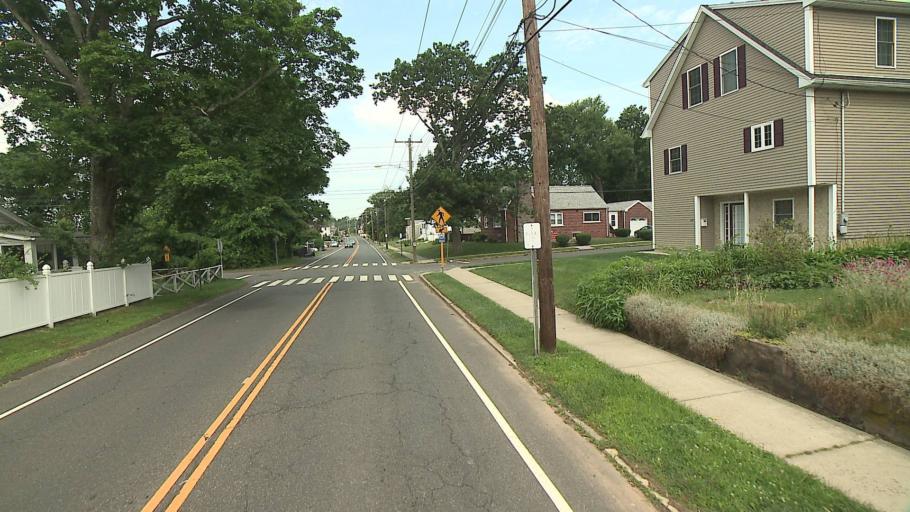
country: US
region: Connecticut
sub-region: New Haven County
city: Woodmont
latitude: 41.2355
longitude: -72.9811
